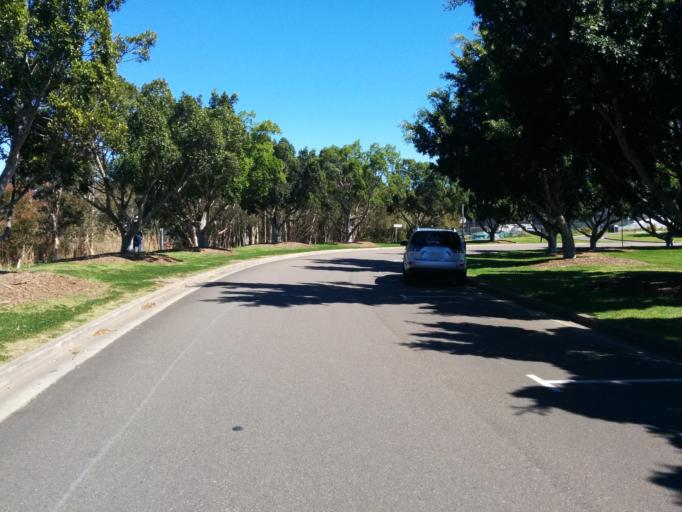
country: AU
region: New South Wales
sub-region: Canada Bay
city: Concord West
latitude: -33.8502
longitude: 151.0766
